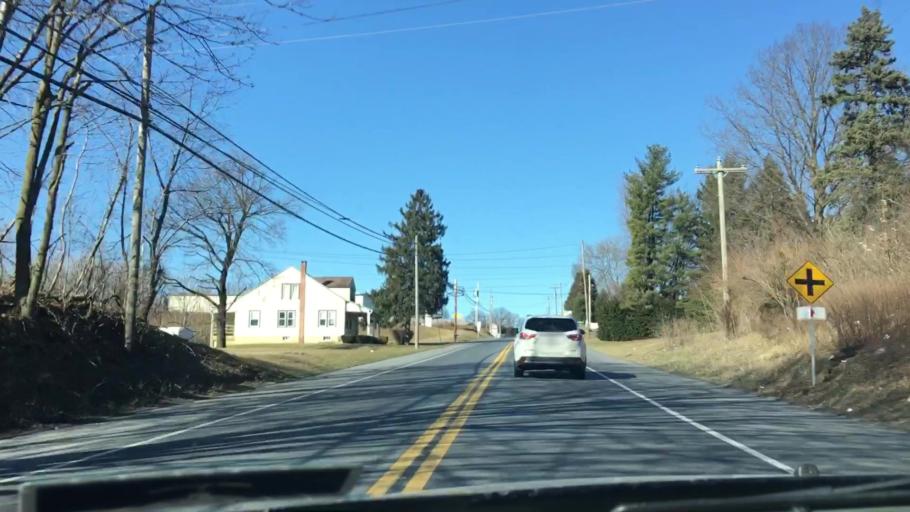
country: US
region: Pennsylvania
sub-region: Lancaster County
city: Akron
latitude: 40.1435
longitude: -76.2102
